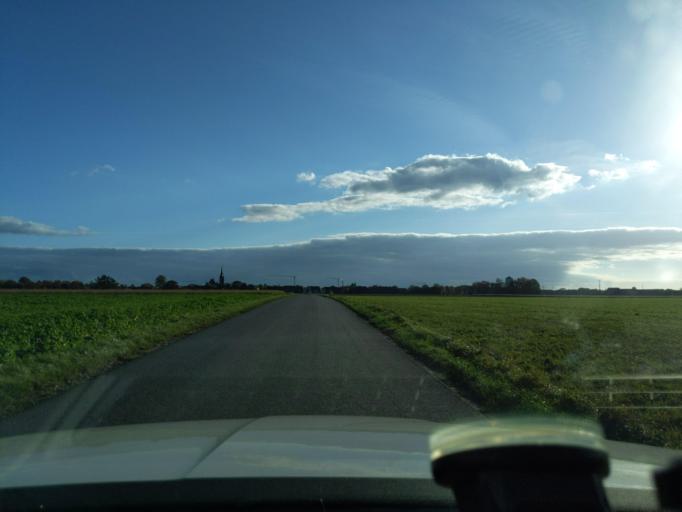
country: DE
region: North Rhine-Westphalia
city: Kempen
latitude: 51.3926
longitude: 6.4516
